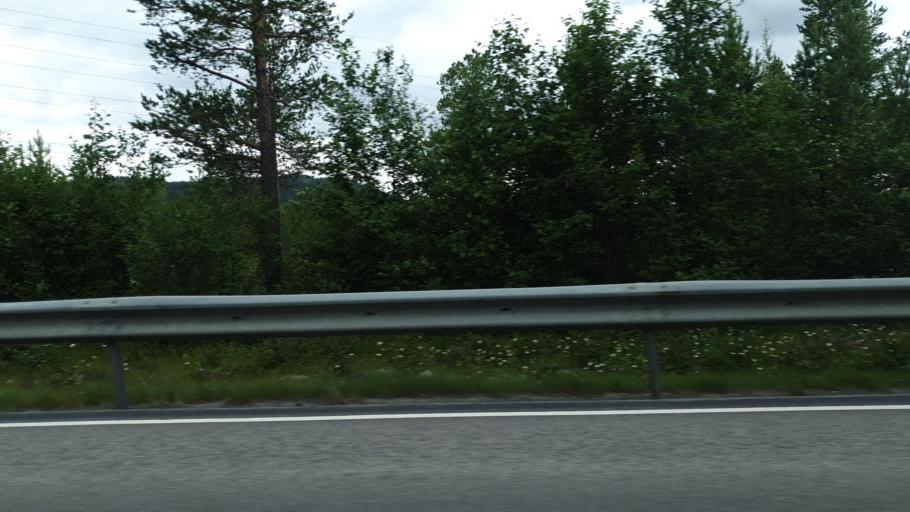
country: NO
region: Sor-Trondelag
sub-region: Rennebu
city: Berkak
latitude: 62.7948
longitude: 10.0155
